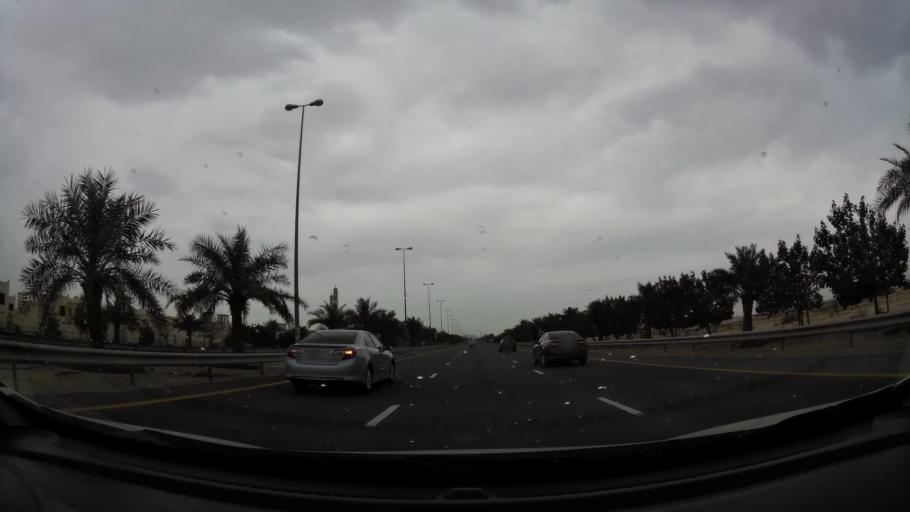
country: BH
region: Central Governorate
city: Madinat Hamad
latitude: 26.0902
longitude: 50.5394
